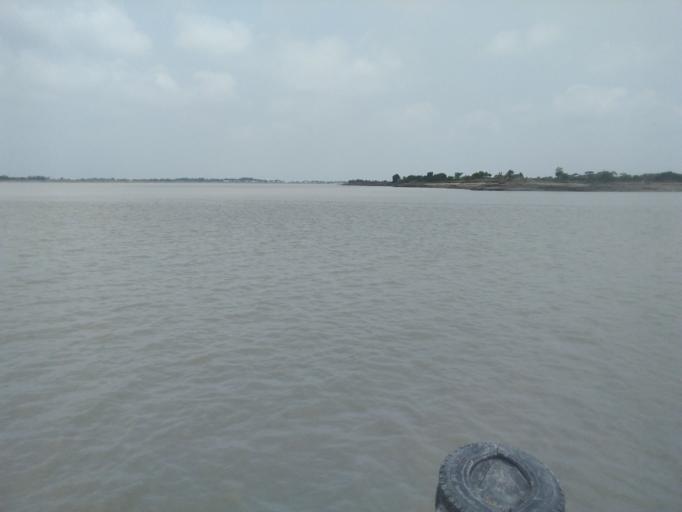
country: BD
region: Khulna
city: Phultala
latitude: 22.6440
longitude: 89.4119
